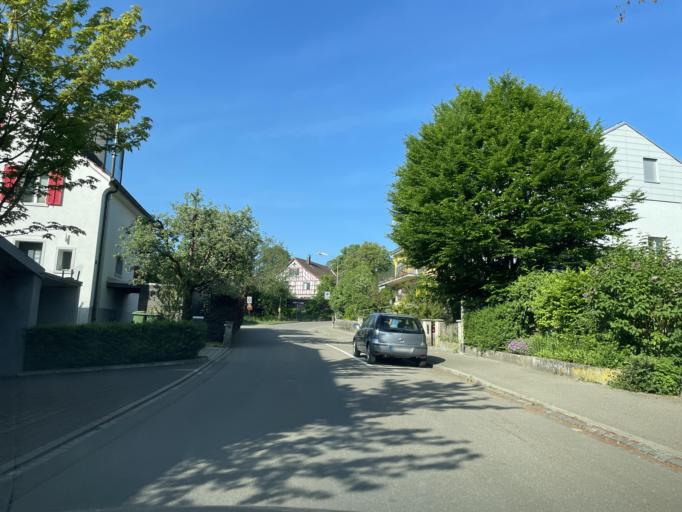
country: CH
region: Zurich
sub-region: Bezirk Winterthur
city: Veltheim
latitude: 47.5122
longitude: 8.7172
